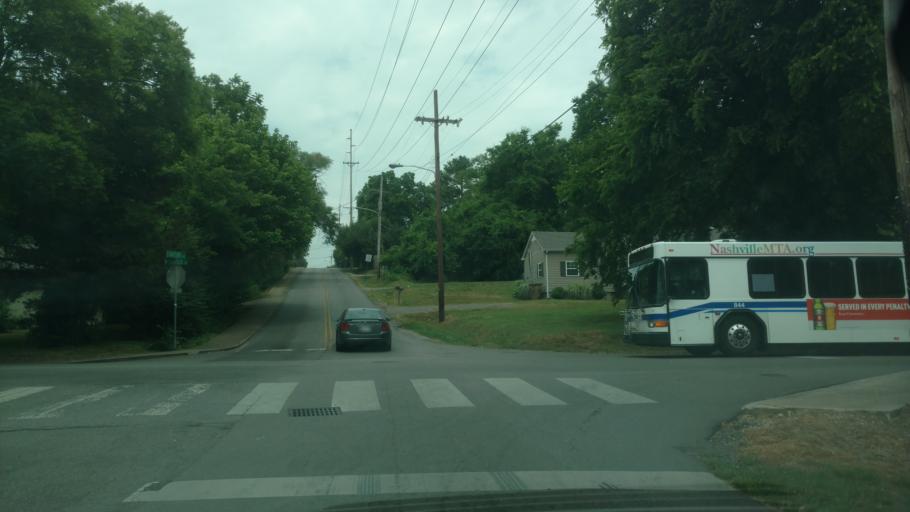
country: US
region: Tennessee
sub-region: Davidson County
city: Nashville
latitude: 36.2078
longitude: -86.7170
